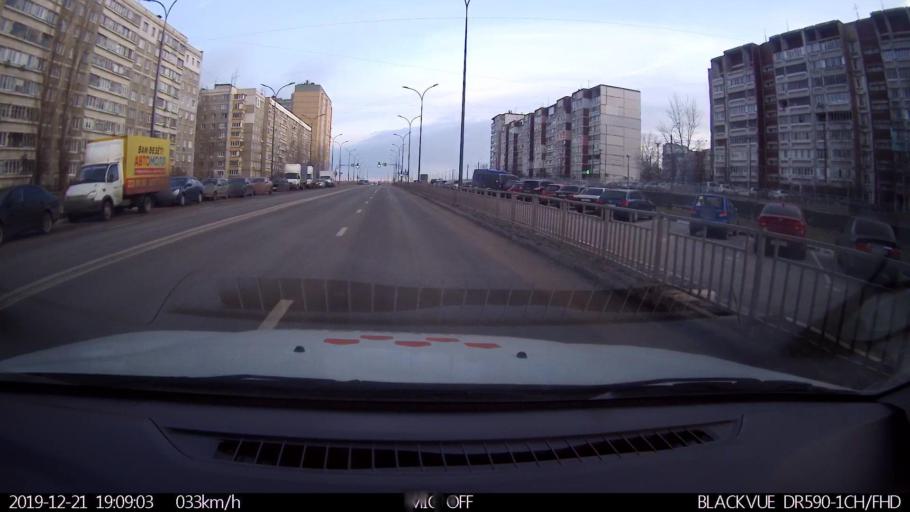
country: RU
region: Nizjnij Novgorod
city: Nizhniy Novgorod
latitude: 56.3445
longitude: 43.9330
